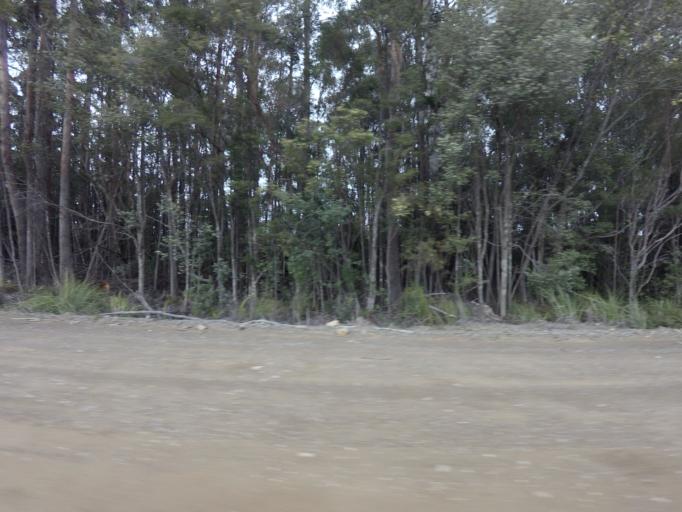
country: AU
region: Tasmania
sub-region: Huon Valley
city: Geeveston
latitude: -43.4884
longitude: 146.8902
